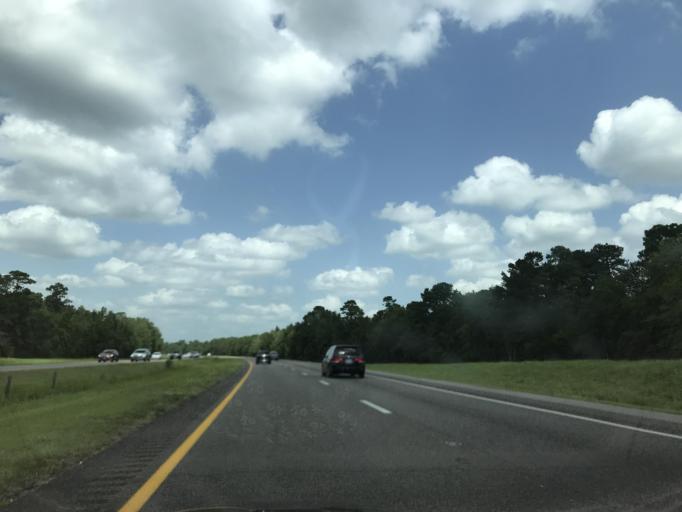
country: US
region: North Carolina
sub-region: Pender County
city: Burgaw
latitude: 34.5042
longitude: -77.8767
